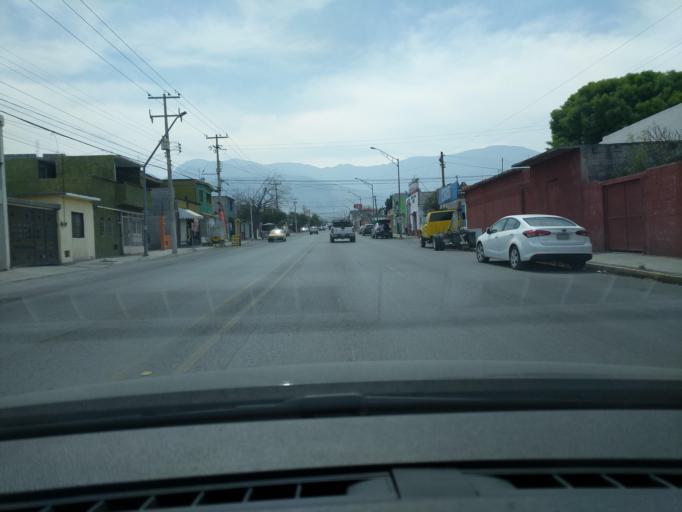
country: MX
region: Coahuila
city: Saltillo
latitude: 25.4159
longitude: -100.9427
